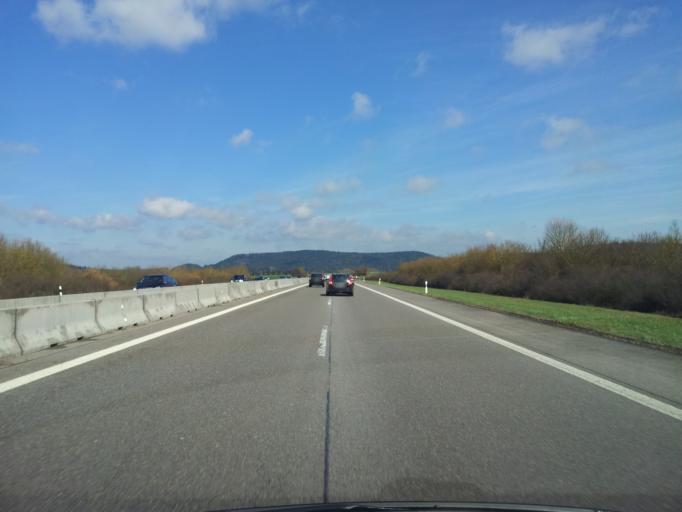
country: DE
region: Baden-Wuerttemberg
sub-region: Freiburg Region
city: Epfendorf
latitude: 48.2563
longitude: 8.6425
